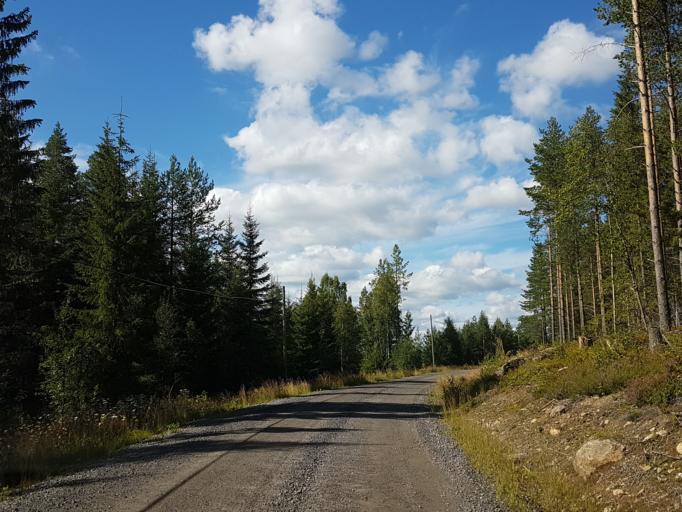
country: SE
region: Vaesterbotten
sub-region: Skelleftea Kommun
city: Burtraesk
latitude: 64.2752
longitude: 20.4804
